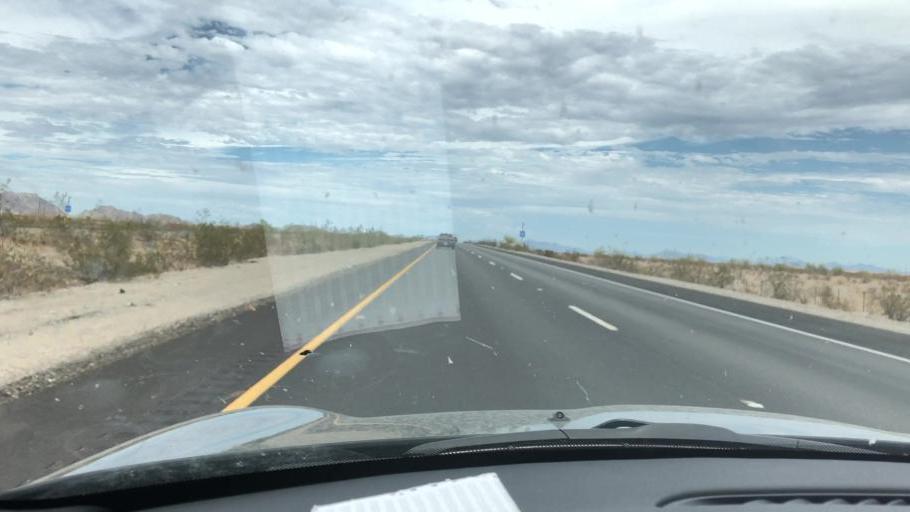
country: US
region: California
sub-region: Riverside County
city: Mesa Verde
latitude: 33.6096
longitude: -114.8318
